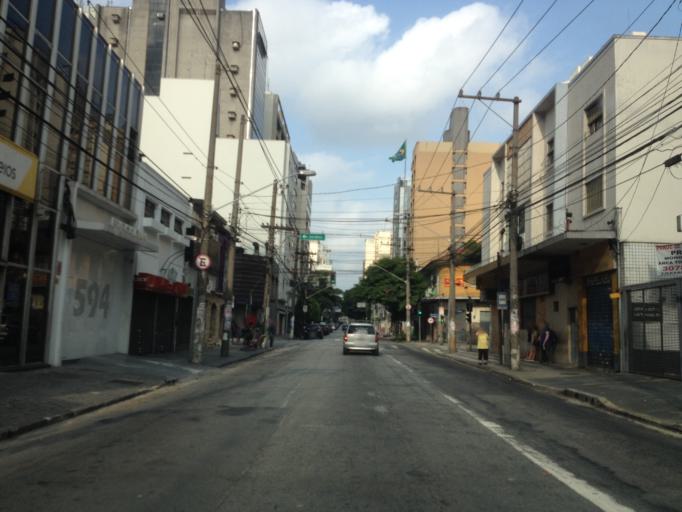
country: BR
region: Sao Paulo
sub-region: Sao Paulo
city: Sao Paulo
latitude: -23.5833
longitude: -46.6766
